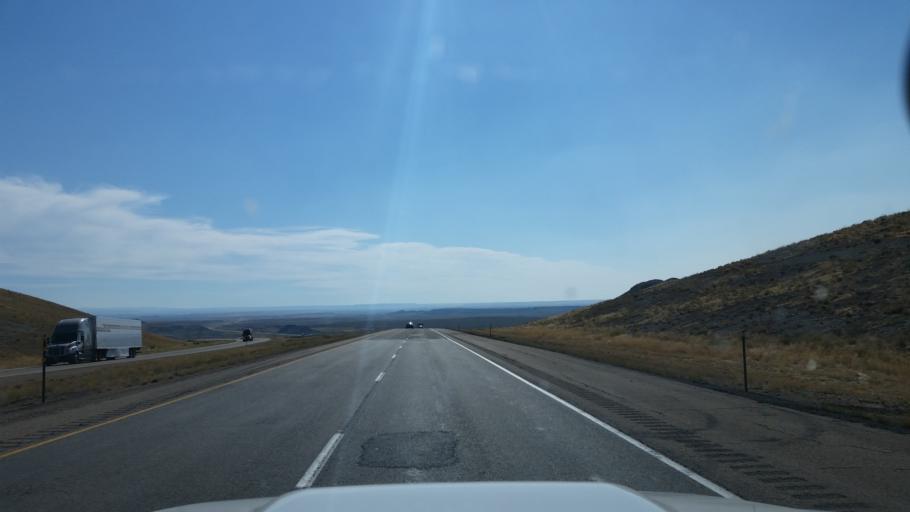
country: US
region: Wyoming
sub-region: Uinta County
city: Lyman
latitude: 41.4297
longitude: -110.1191
